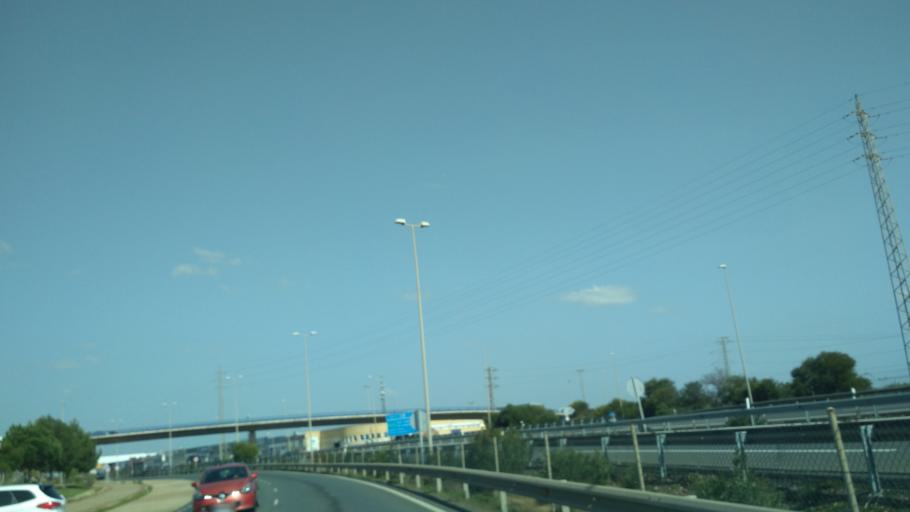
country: ES
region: Andalusia
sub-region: Provincia de Huelva
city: Huelva
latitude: 37.2588
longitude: -6.9217
